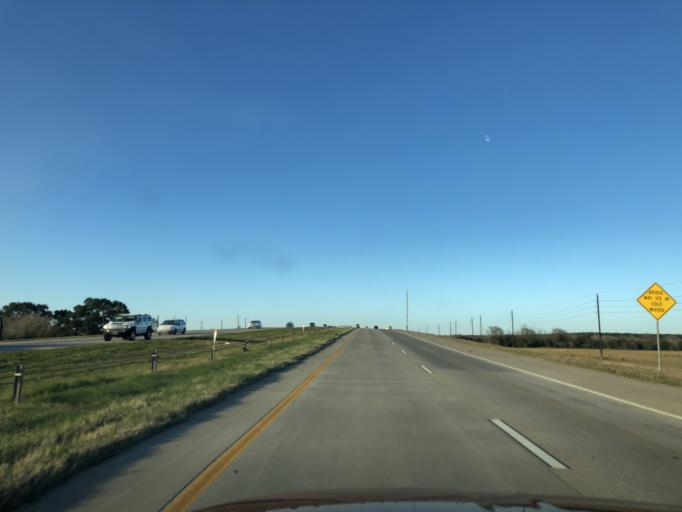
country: US
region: Texas
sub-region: Harris County
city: Katy
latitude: 29.8577
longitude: -95.7559
